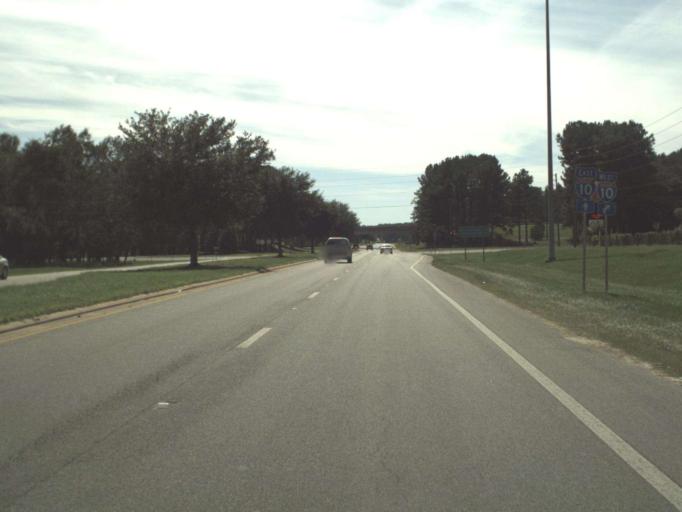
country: US
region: Florida
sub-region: Washington County
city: Chipley
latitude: 30.7511
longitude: -85.5510
